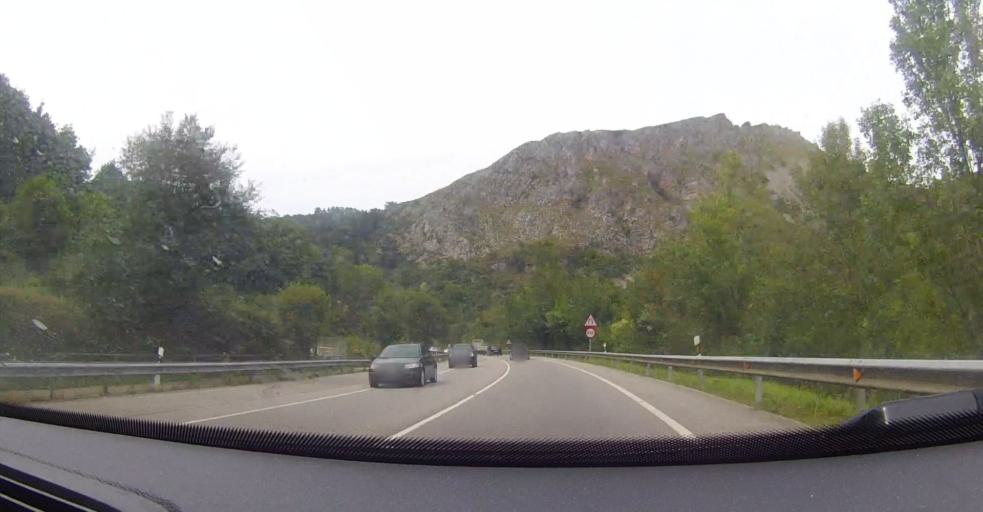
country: ES
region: Asturias
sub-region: Province of Asturias
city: Parres
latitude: 43.3697
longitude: -5.1483
